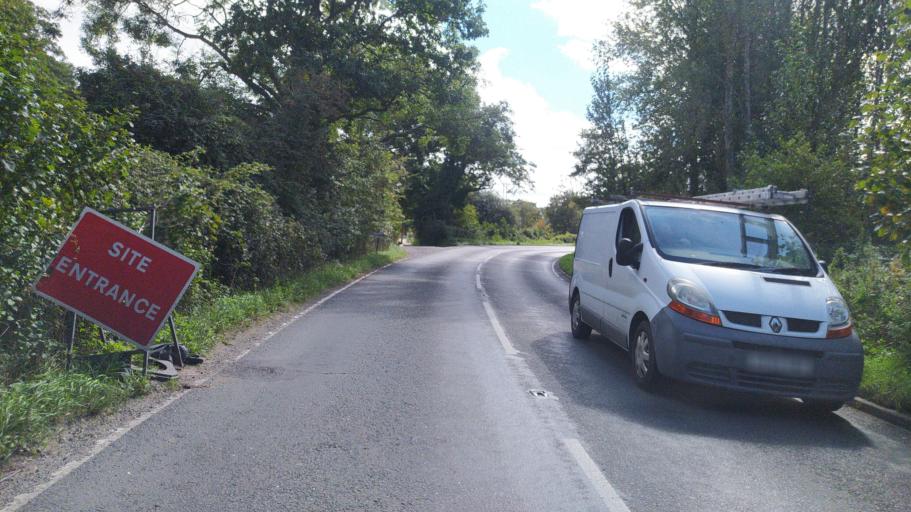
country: GB
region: England
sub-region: Hampshire
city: Romsey
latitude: 51.0102
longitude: -1.5000
